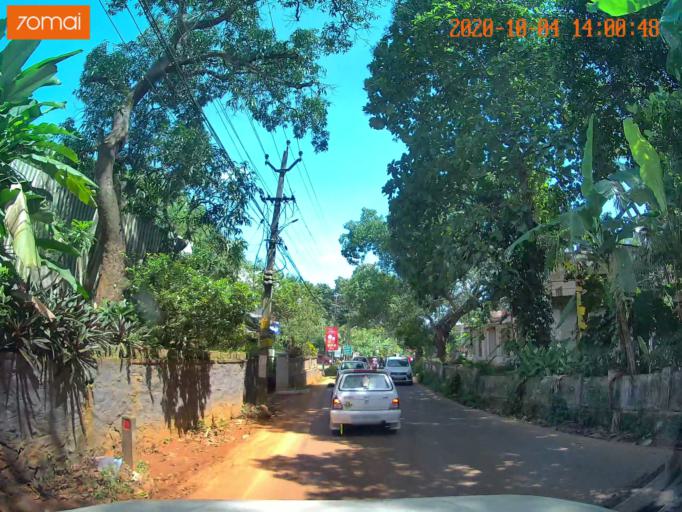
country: IN
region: Kerala
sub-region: Kottayam
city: Lalam
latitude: 9.7120
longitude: 76.6706
